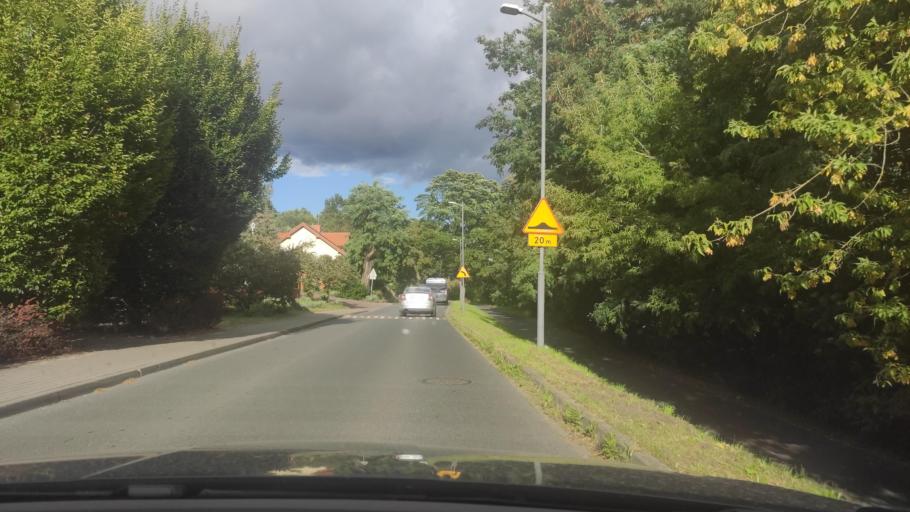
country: PL
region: Greater Poland Voivodeship
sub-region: Powiat poznanski
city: Swarzedz
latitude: 52.4093
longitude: 17.0469
